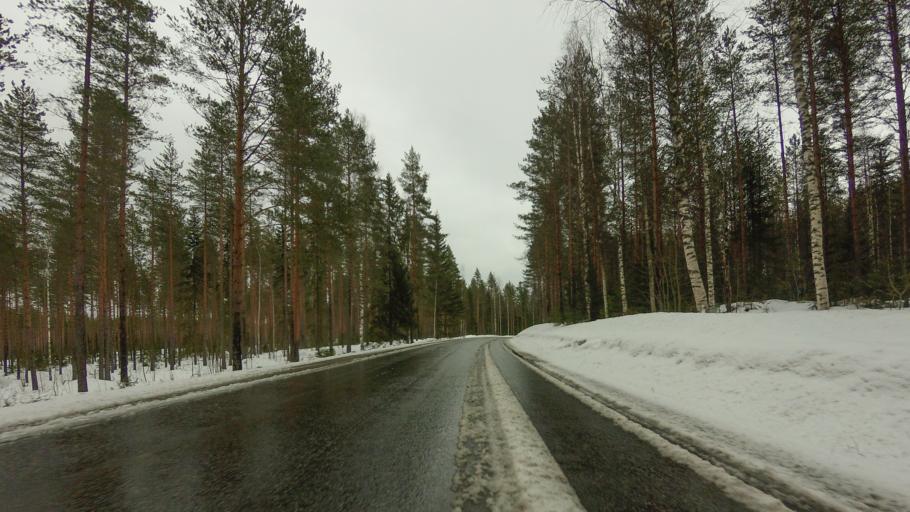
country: FI
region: Southern Savonia
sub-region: Savonlinna
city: Savonlinna
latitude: 61.9840
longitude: 28.8059
